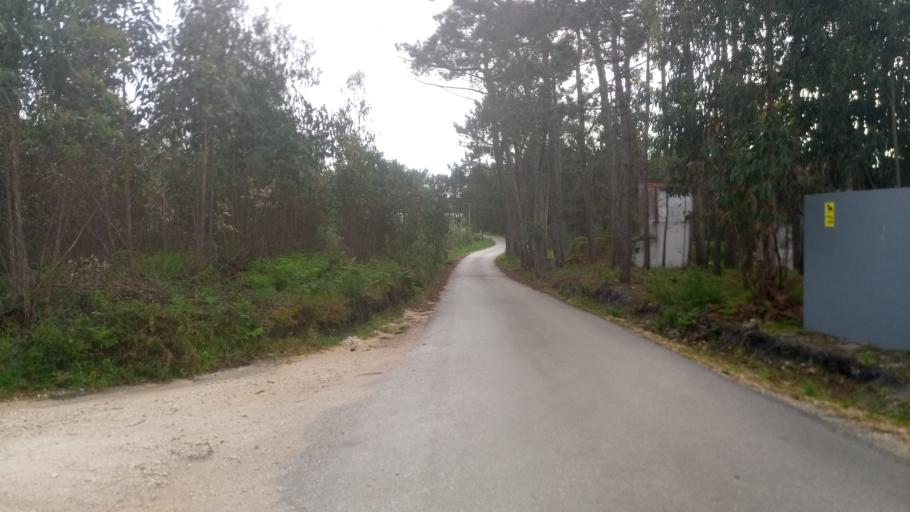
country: PT
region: Leiria
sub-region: Caldas da Rainha
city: Caldas da Rainha
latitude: 39.4383
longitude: -9.1603
